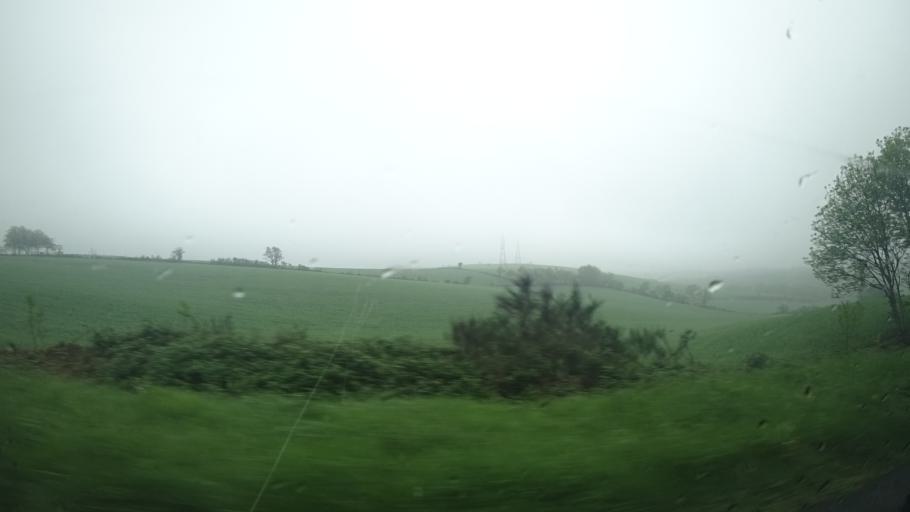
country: FR
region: Midi-Pyrenees
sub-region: Departement de l'Aveyron
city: Laissac
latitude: 44.3274
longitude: 2.7866
